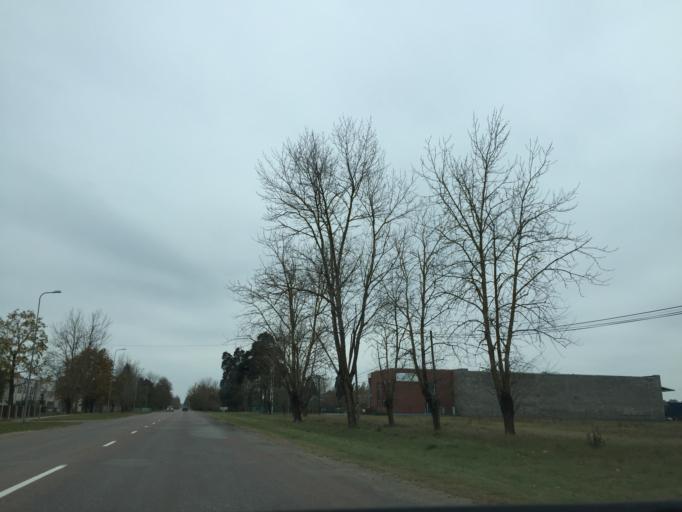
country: LV
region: Marupe
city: Marupe
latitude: 56.8868
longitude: 24.0710
